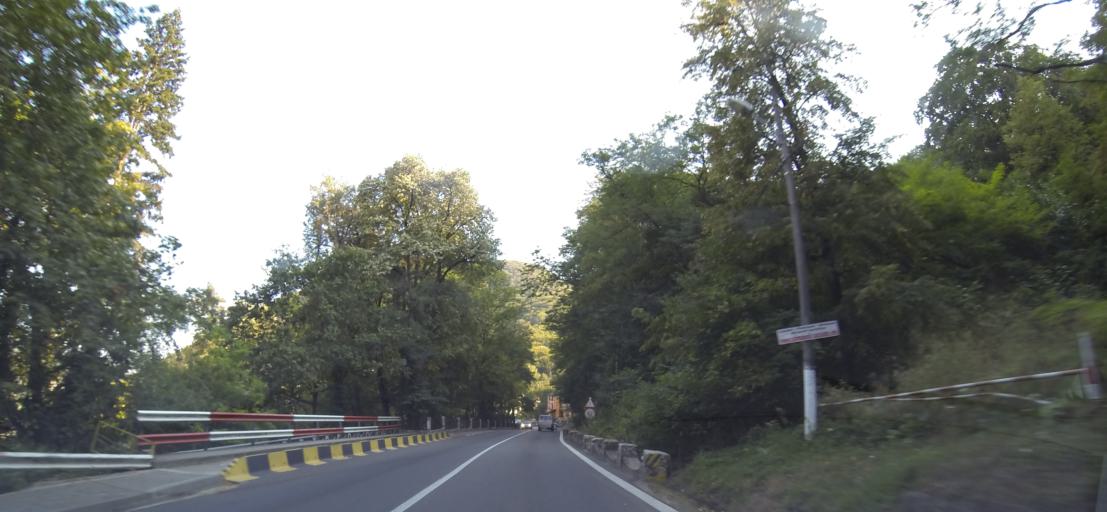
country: RO
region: Valcea
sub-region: Oras Calimanesti
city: Calimanesti
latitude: 45.2616
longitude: 24.3190
